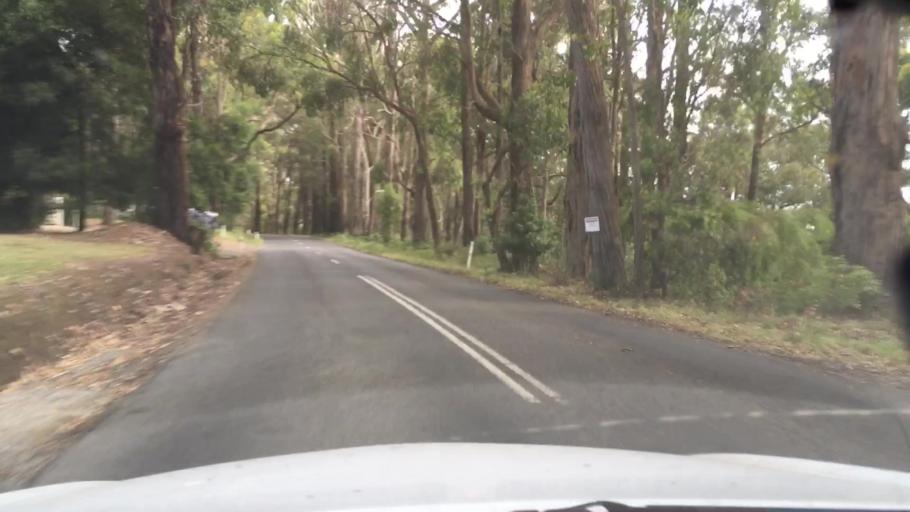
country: AU
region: Victoria
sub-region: Cardinia
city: Cockatoo
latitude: -37.9160
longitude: 145.4704
